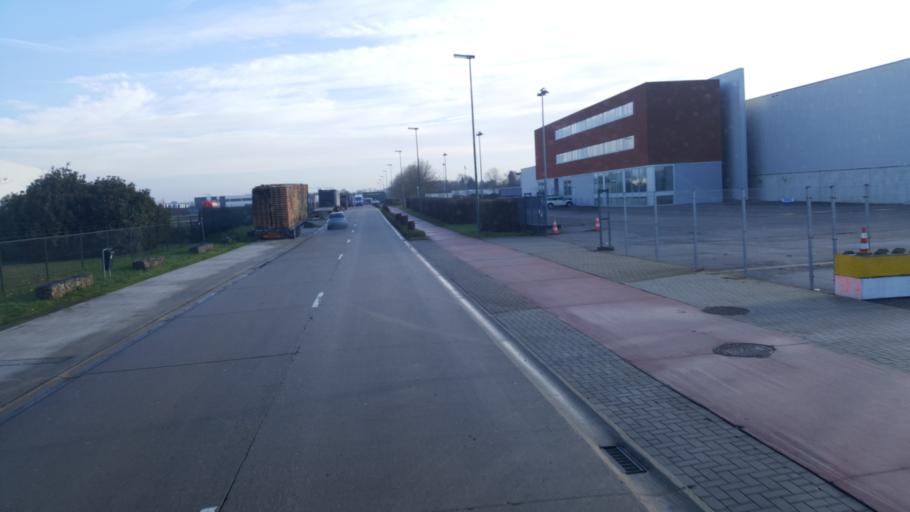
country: BE
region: Flanders
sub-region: Provincie Limburg
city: Maasmechelen
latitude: 50.9413
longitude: 5.6977
